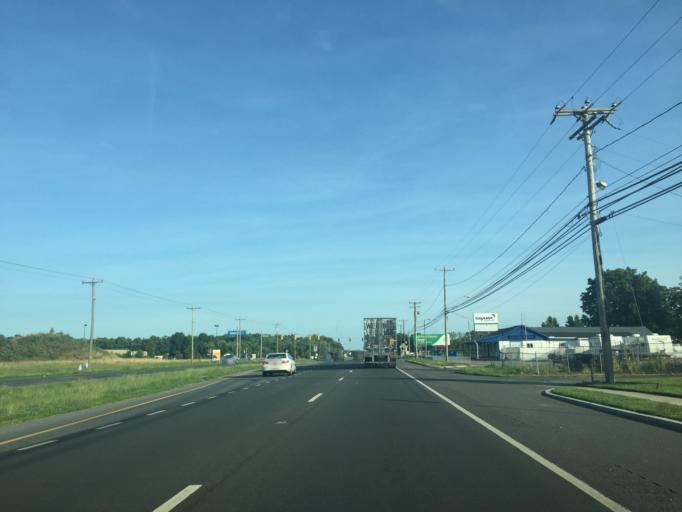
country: US
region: Delaware
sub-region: Kent County
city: Cheswold
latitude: 39.2188
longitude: -75.5744
